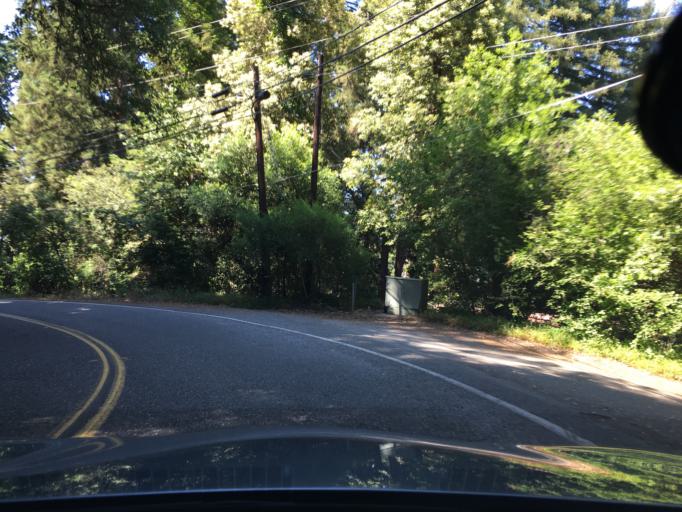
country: US
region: California
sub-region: Santa Clara County
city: Lexington Hills
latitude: 37.1595
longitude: -121.9800
